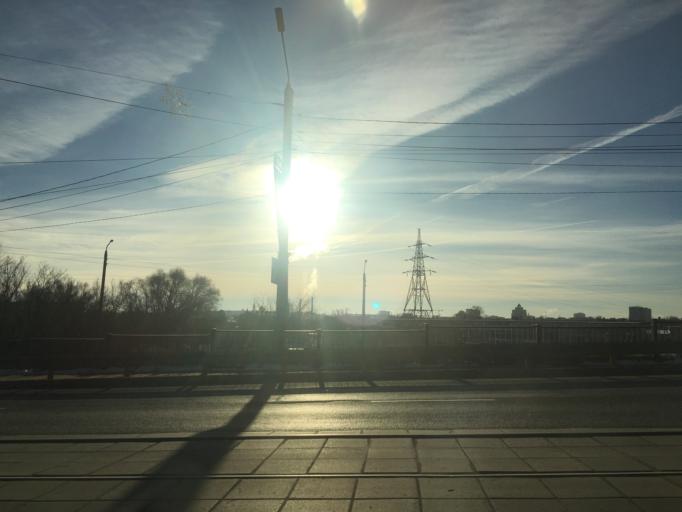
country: RU
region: Tula
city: Tula
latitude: 54.2027
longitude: 37.6250
